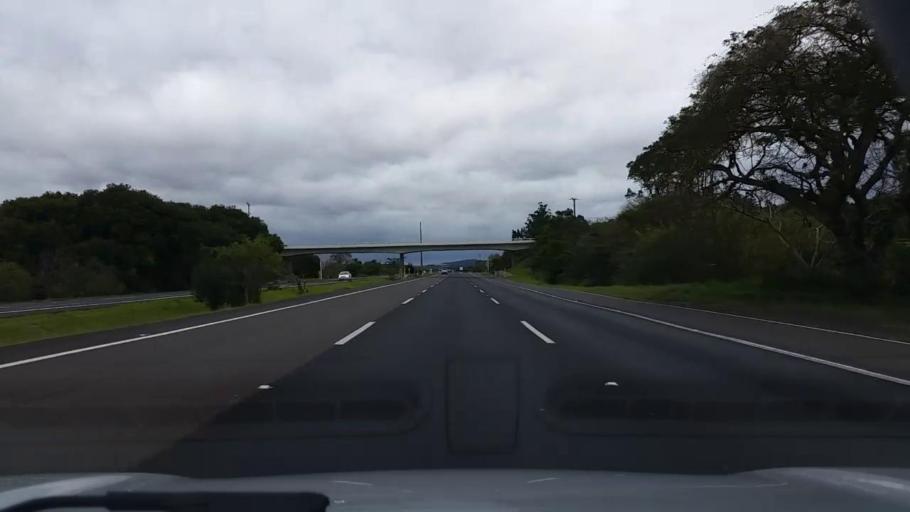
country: BR
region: Rio Grande do Sul
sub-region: Osorio
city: Osorio
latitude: -29.8749
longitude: -50.4242
